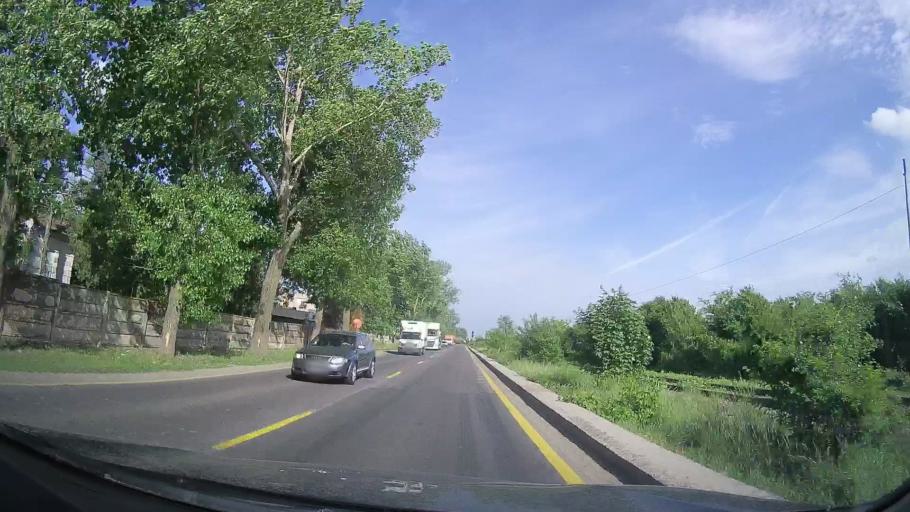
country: RO
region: Ilfov
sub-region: Comuna Magurele
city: Magurele
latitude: 44.3641
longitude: 26.0228
